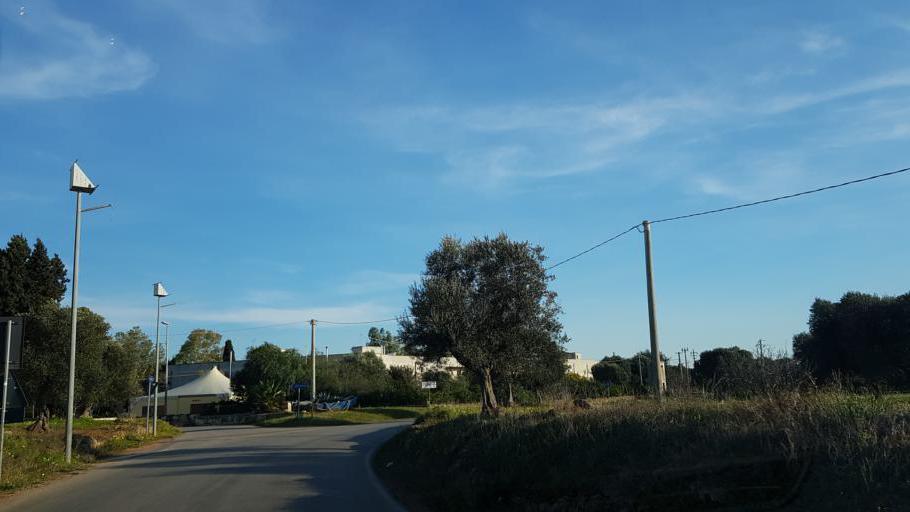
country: IT
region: Apulia
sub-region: Provincia di Brindisi
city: San Vito dei Normanni
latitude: 40.6935
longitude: 17.7613
